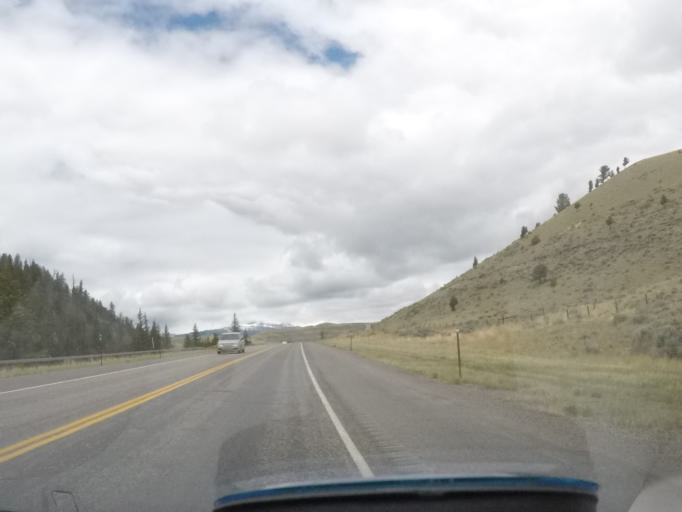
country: US
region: Wyoming
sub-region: Sublette County
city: Pinedale
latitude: 43.5798
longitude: -109.7623
